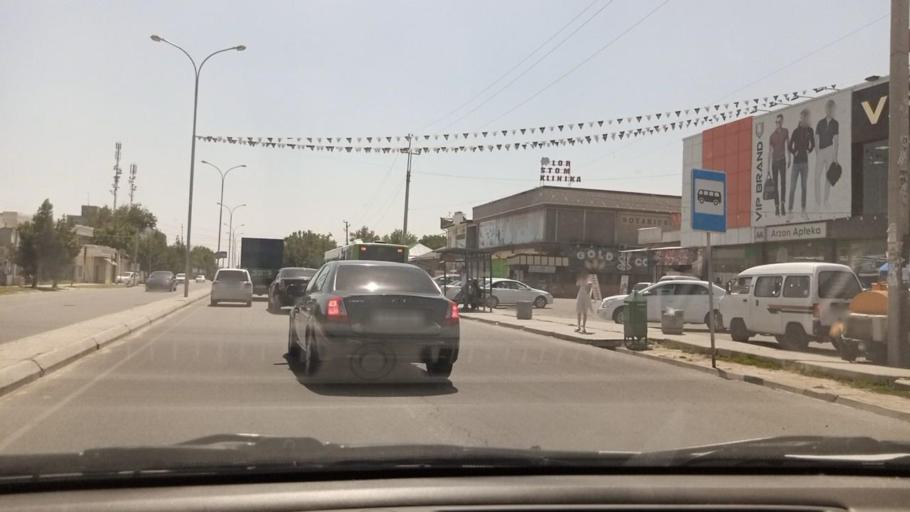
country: UZ
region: Toshkent
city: Urtaowul
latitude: 41.2261
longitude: 69.1795
